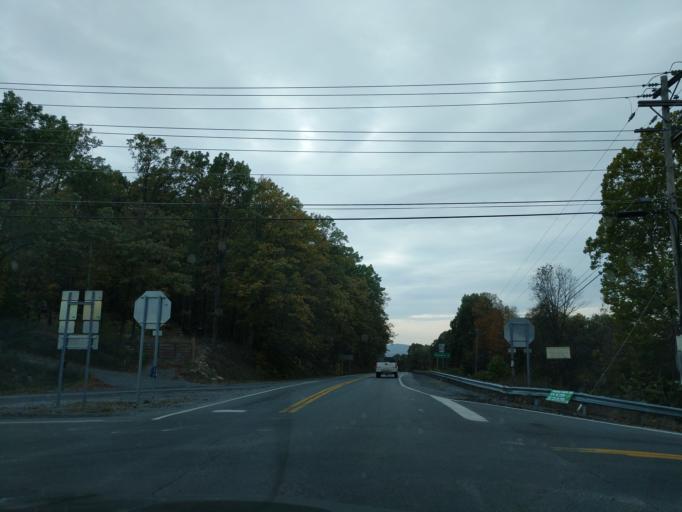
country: US
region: West Virginia
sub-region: Berkeley County
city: Inwood
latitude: 39.3896
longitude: -78.1097
